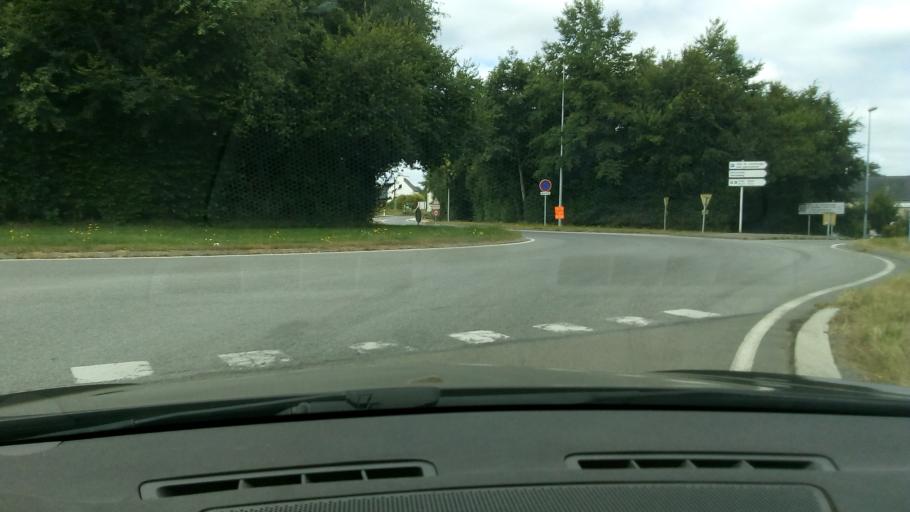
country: FR
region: Brittany
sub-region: Departement du Finistere
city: Concarneau
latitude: 47.9217
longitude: -3.9007
